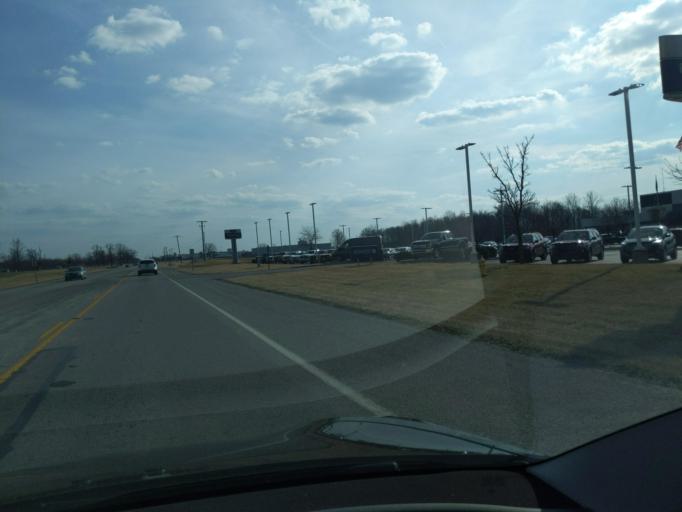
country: US
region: Ohio
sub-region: Allen County
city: Lima
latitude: 40.7225
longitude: -84.0707
